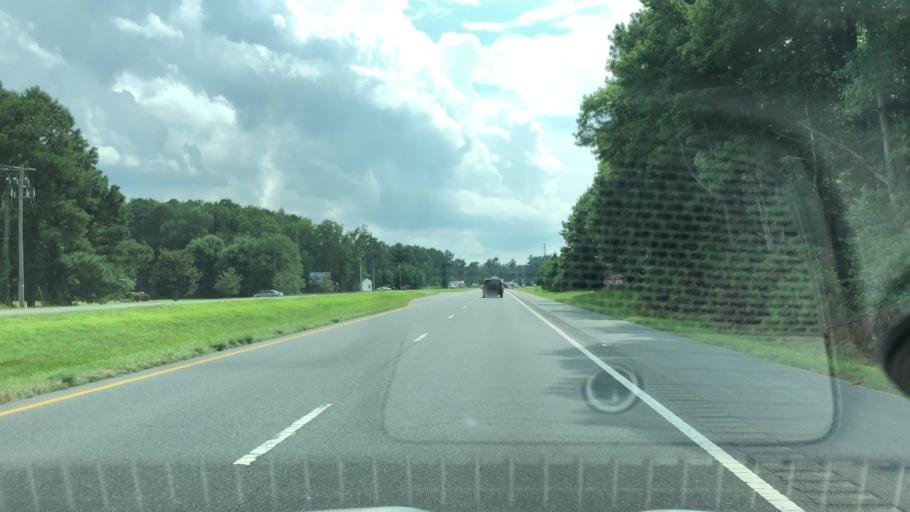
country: US
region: Virginia
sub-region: Accomack County
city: Accomac
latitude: 37.7103
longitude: -75.6945
